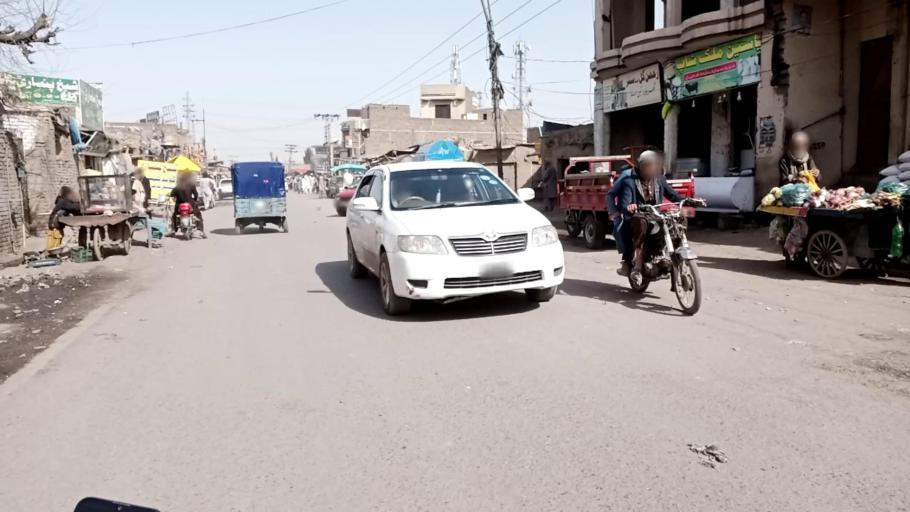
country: PK
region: Khyber Pakhtunkhwa
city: Peshawar
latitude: 33.9830
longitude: 71.6338
